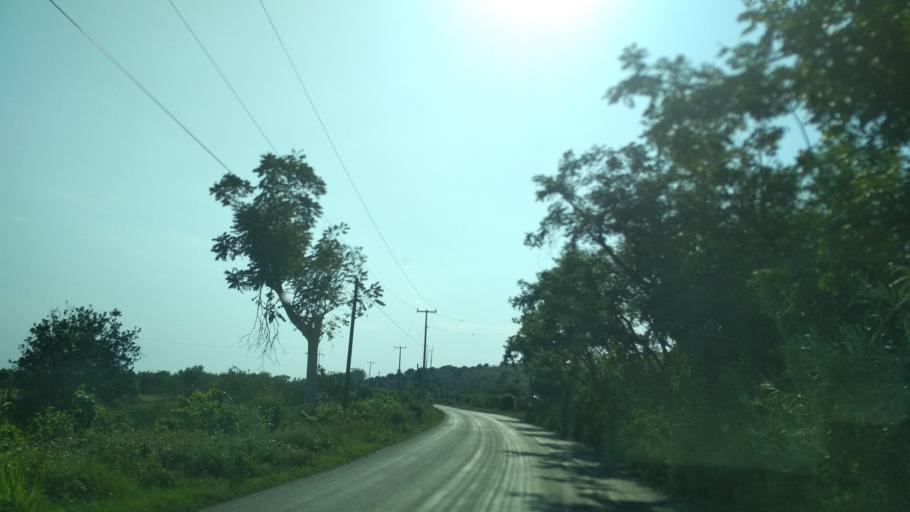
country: MX
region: Veracruz
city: Agua Dulce
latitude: 20.3929
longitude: -97.2784
